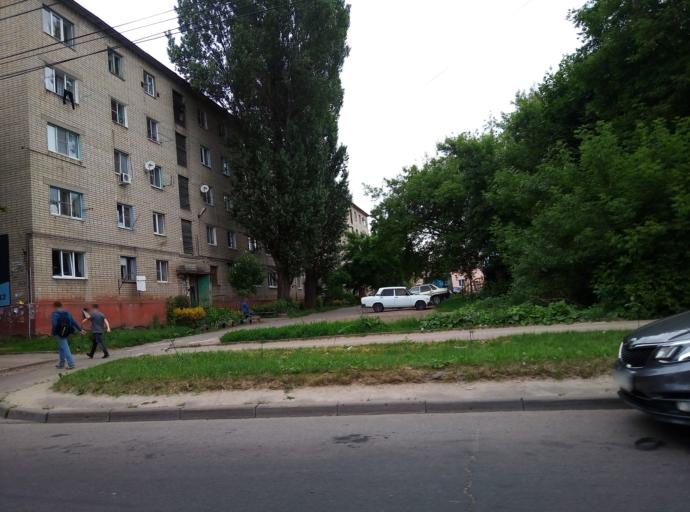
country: RU
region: Kursk
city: Kursk
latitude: 51.7103
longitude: 36.1457
